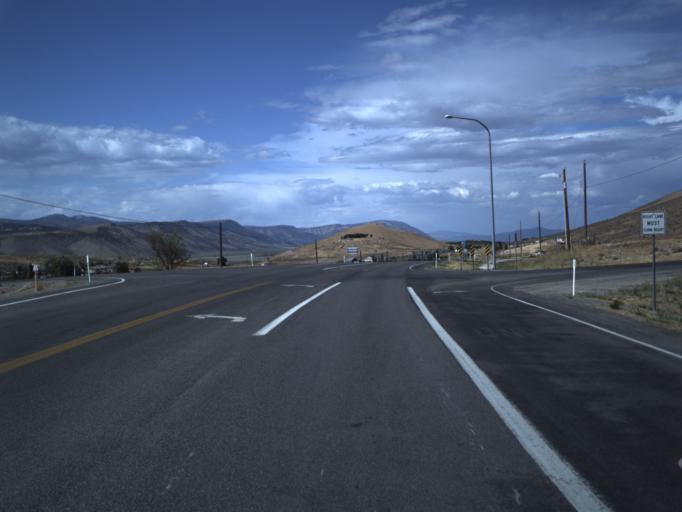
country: US
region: Utah
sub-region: Sanpete County
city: Manti
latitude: 39.1982
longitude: -111.6926
